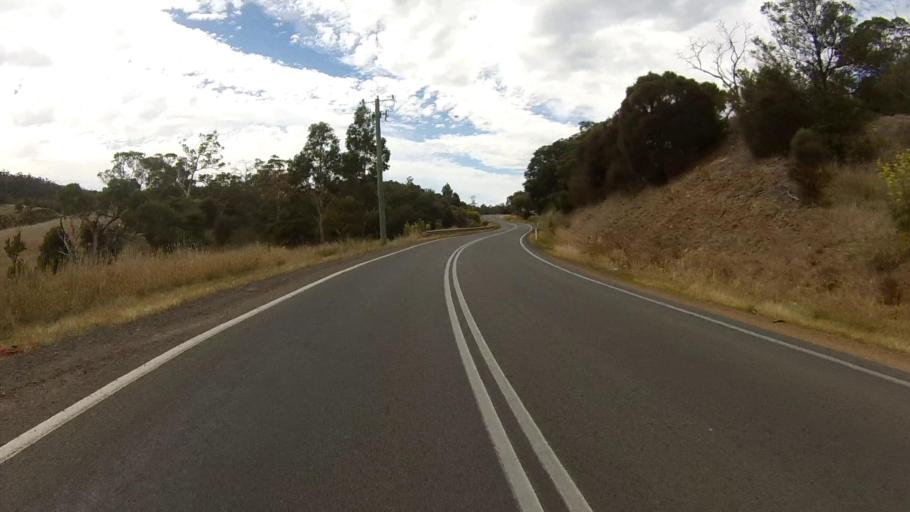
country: AU
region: Tasmania
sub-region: Sorell
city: Sorell
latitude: -42.6958
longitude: 147.4796
